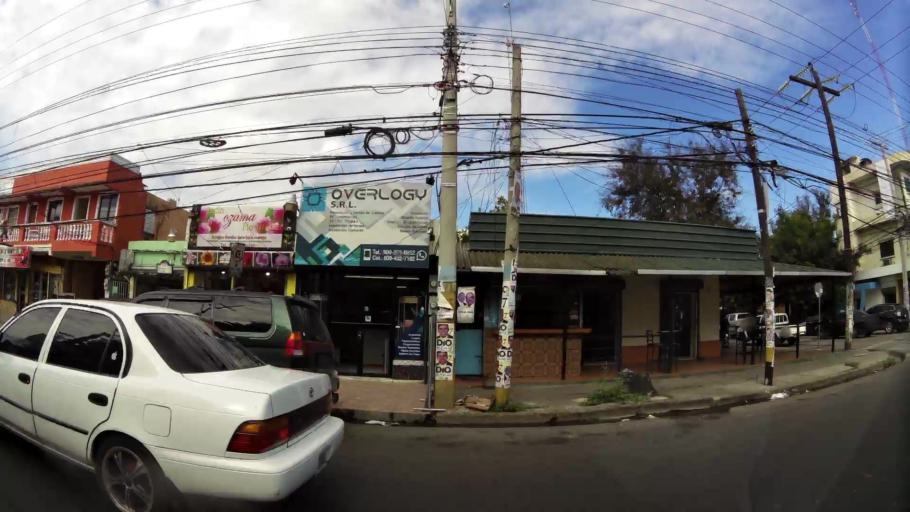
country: DO
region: Santo Domingo
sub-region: Santo Domingo
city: Santo Domingo Este
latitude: 18.4932
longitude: -69.8651
